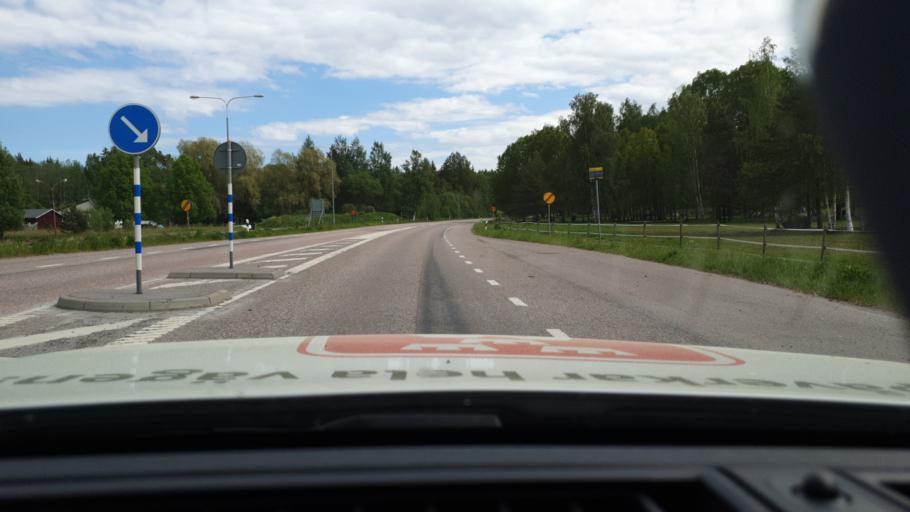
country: SE
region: Uppsala
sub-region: Alvkarleby Kommun
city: AElvkarleby
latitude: 60.6015
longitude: 17.4547
